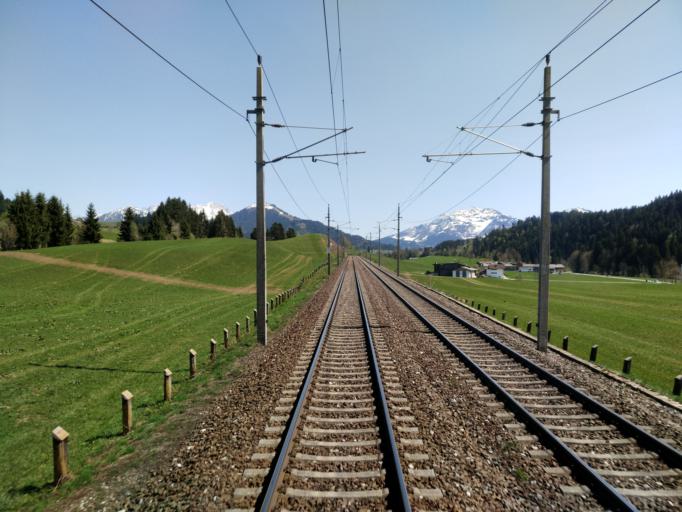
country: AT
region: Tyrol
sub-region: Politischer Bezirk Kitzbuhel
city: Fieberbrunn
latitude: 47.4978
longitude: 12.4978
